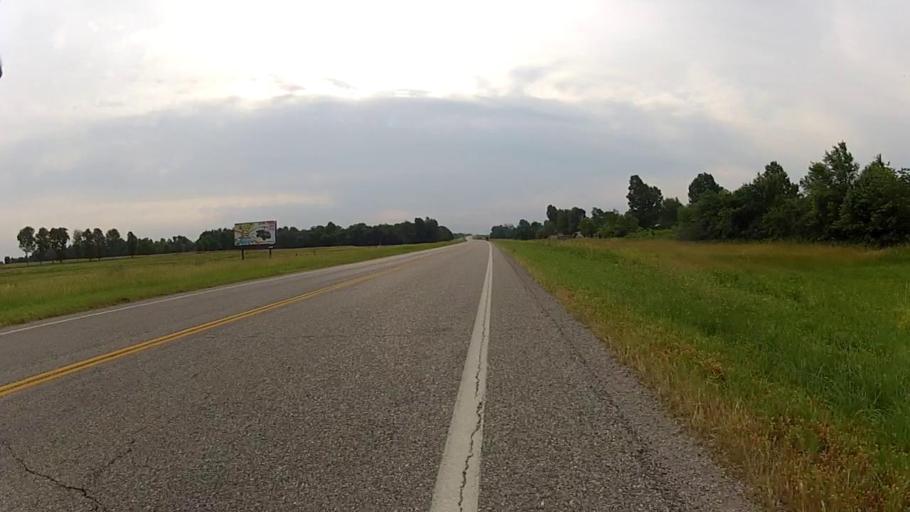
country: US
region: Kansas
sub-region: Cherokee County
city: Columbus
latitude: 37.1784
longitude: -94.8490
